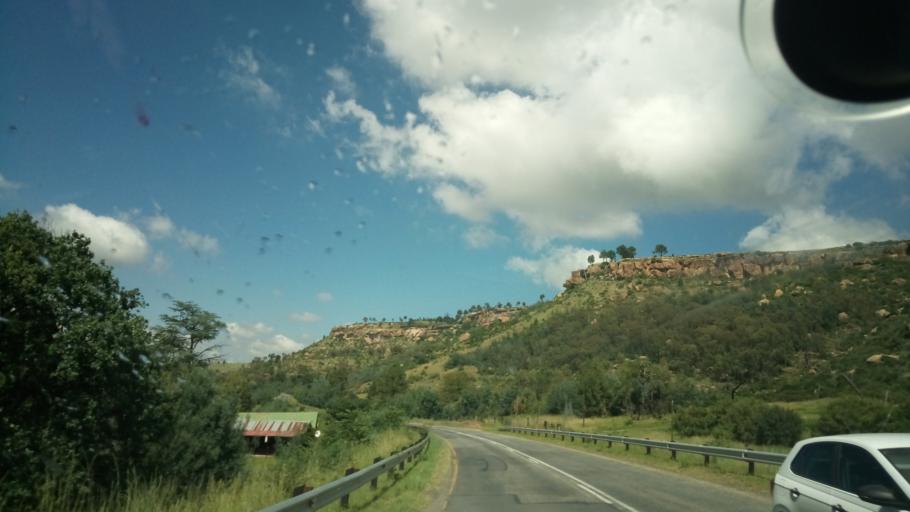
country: ZA
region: Orange Free State
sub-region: Thabo Mofutsanyana District Municipality
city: Ficksburg
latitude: -28.8649
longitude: 27.8715
